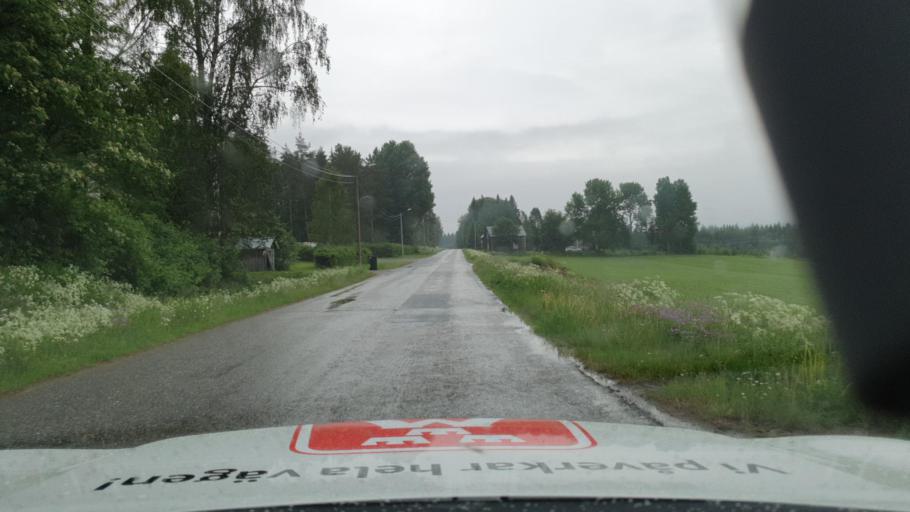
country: SE
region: Vaesterbotten
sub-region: Nordmalings Kommun
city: Nordmaling
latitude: 63.7998
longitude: 19.5048
